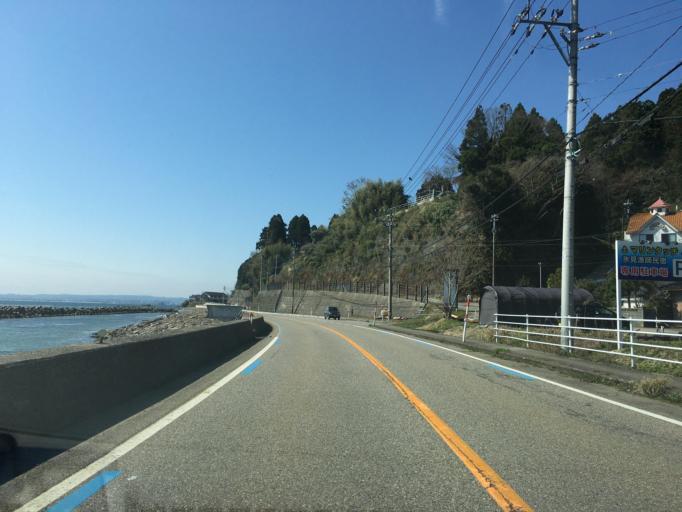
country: JP
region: Toyama
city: Himi
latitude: 36.9036
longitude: 137.0134
